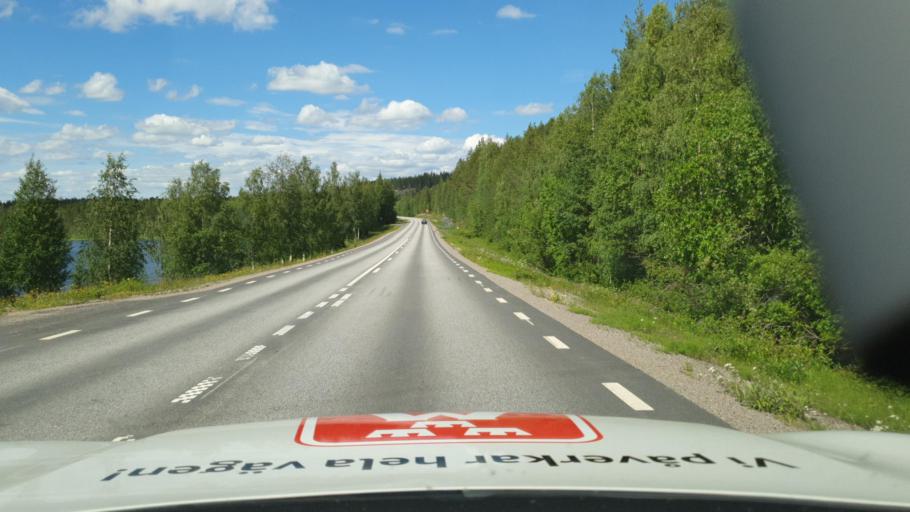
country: SE
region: Vaesterbotten
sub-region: Skelleftea Kommun
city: Langsele
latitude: 64.9611
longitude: 20.2544
